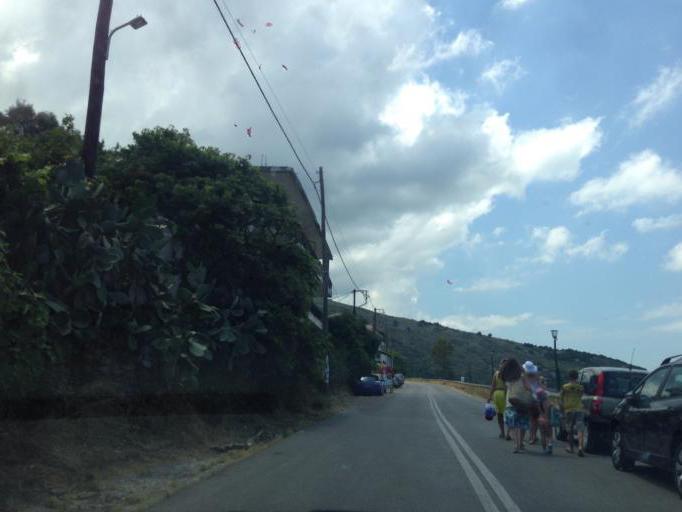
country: GR
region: Ionian Islands
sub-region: Nomos Kerkyras
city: Acharavi
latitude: 39.7880
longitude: 19.9175
